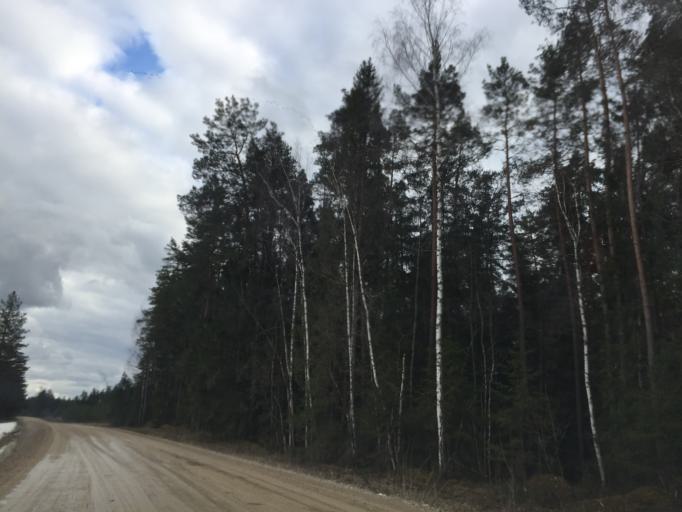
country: LV
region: Ogre
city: Jumprava
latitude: 56.5918
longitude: 24.9881
